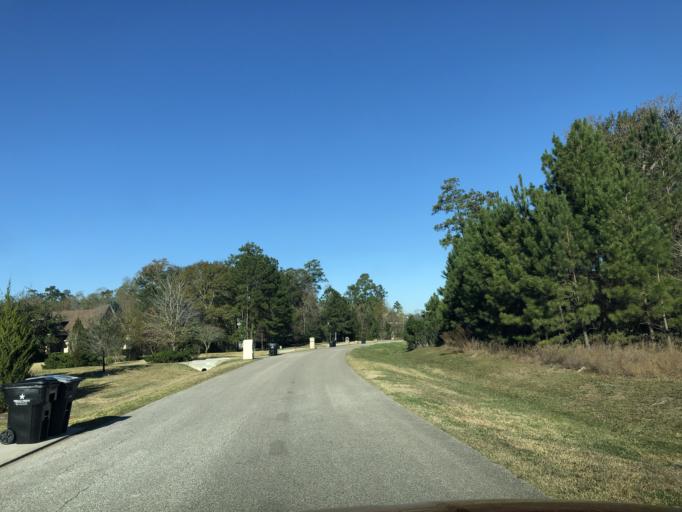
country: US
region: Texas
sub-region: Montgomery County
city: Porter Heights
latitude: 30.0766
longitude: -95.3359
